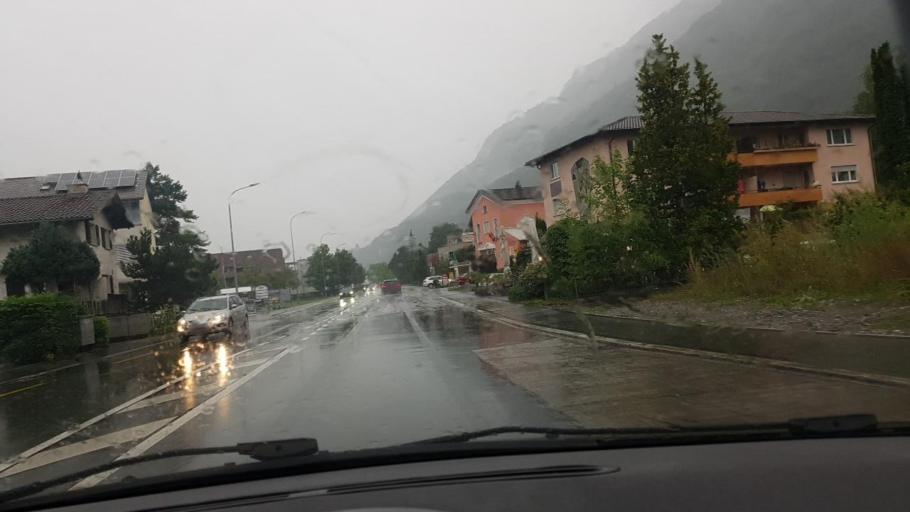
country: LI
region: Triesen
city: Triesen
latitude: 47.1165
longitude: 9.5238
